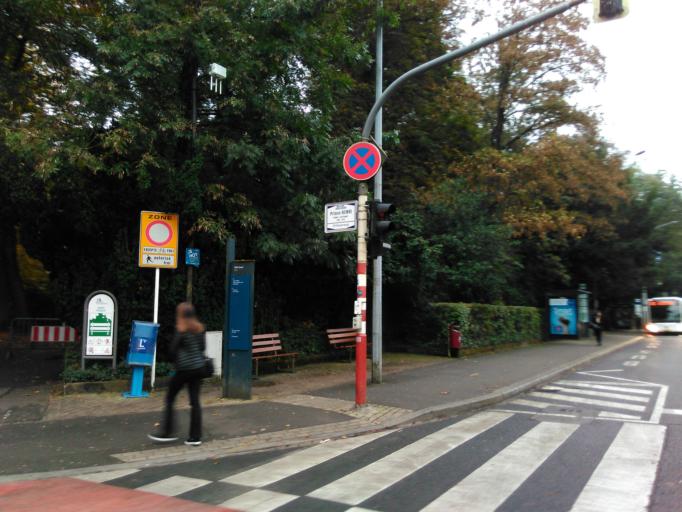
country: LU
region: Luxembourg
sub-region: Canton de Luxembourg
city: Luxembourg
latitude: 49.6123
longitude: 6.1240
